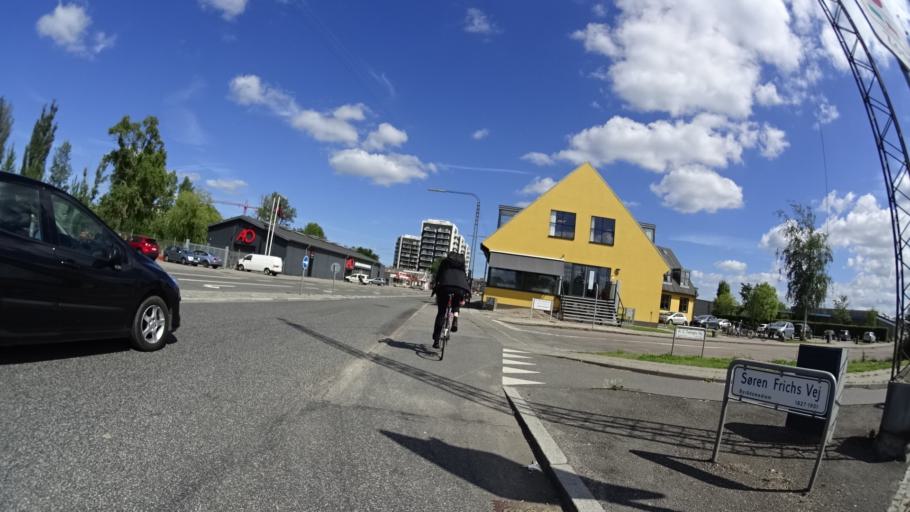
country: DK
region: Central Jutland
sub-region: Arhus Kommune
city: Arhus
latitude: 56.1530
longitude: 10.1828
